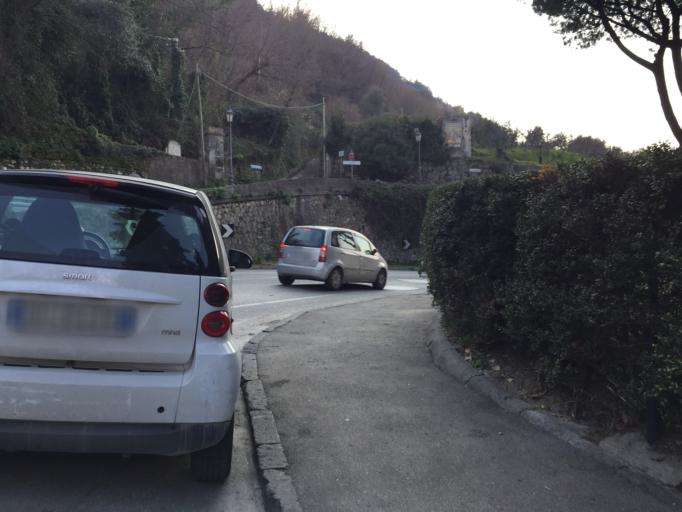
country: IT
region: Campania
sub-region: Provincia di Napoli
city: Castellammare di Stabia
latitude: 40.6881
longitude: 14.4743
